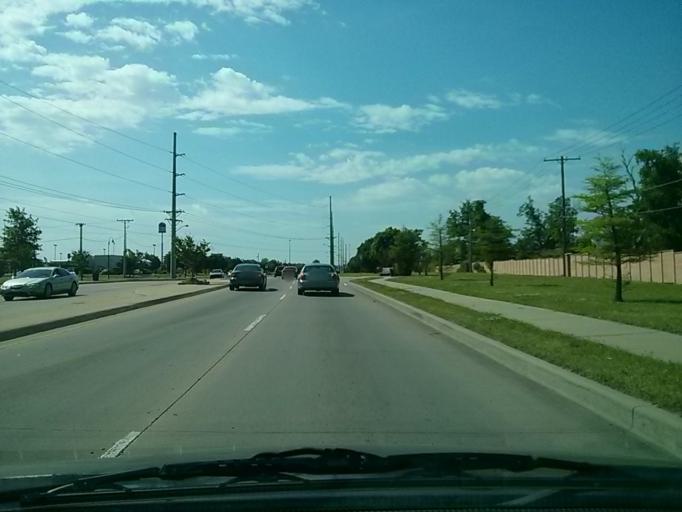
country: US
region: Oklahoma
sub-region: Tulsa County
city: Tulsa
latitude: 36.1812
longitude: -95.9760
